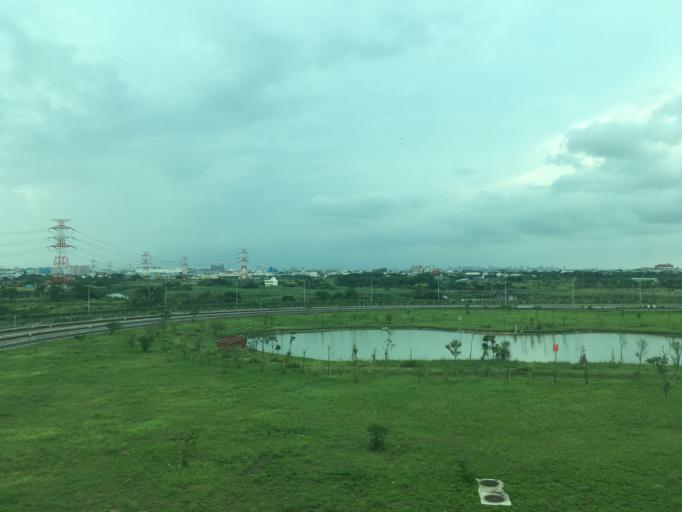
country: TW
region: Taiwan
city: Taoyuan City
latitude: 25.0831
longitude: 121.2728
